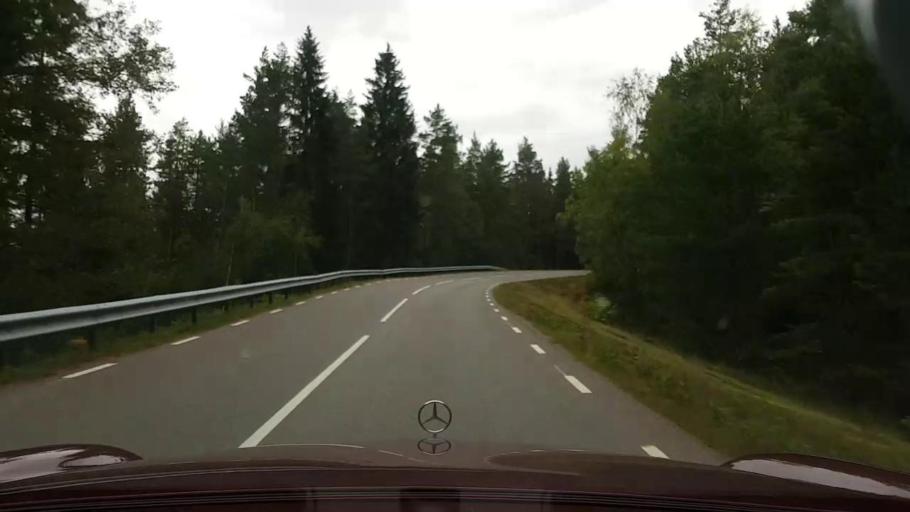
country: SE
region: Vaestra Goetaland
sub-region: Karlsborgs Kommun
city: Karlsborg
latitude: 58.7167
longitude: 14.5022
